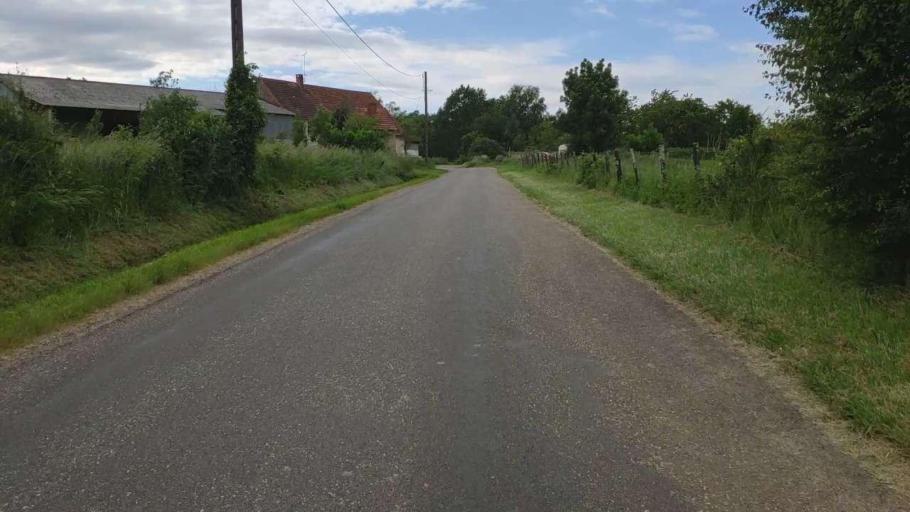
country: FR
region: Franche-Comte
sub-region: Departement du Jura
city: Bletterans
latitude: 46.8062
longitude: 5.5281
